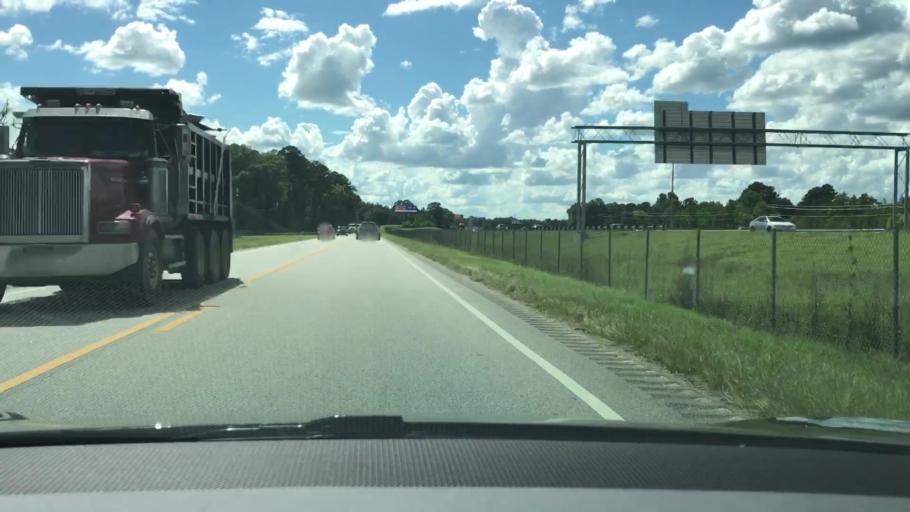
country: US
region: Alabama
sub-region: Montgomery County
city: Pike Road
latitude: 32.3662
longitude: -86.0895
